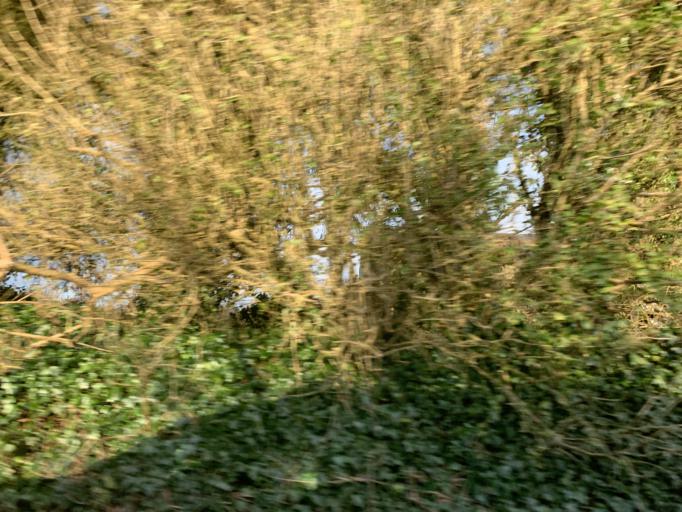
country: IE
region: Connaught
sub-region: Maigh Eo
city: Ballyhaunis
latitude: 53.8185
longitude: -8.6974
